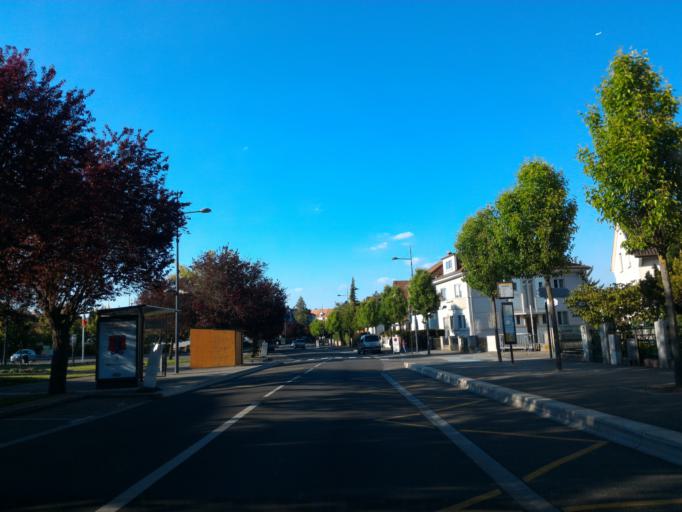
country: FR
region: Alsace
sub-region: Departement du Haut-Rhin
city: Riedisheim
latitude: 47.7443
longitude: 7.3670
